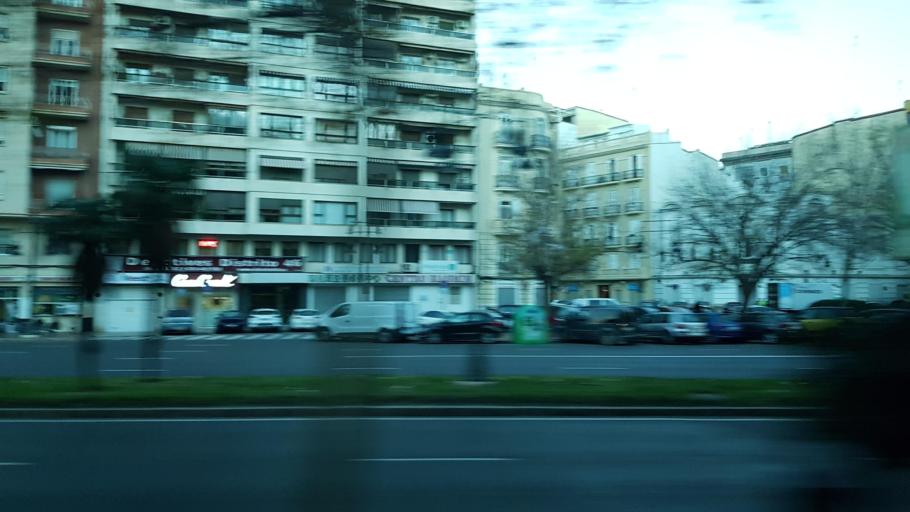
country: ES
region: Valencia
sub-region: Provincia de Valencia
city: Valencia
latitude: 39.4649
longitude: -0.3811
